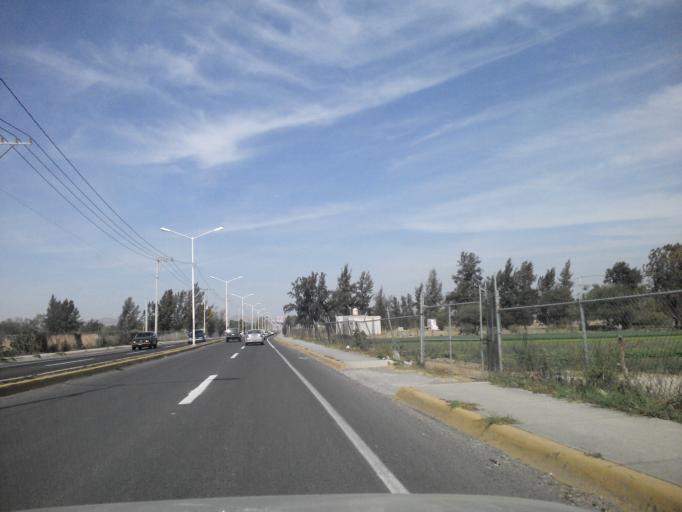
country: MX
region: Jalisco
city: San Sebastian el Grande
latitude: 20.5183
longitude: -103.4102
